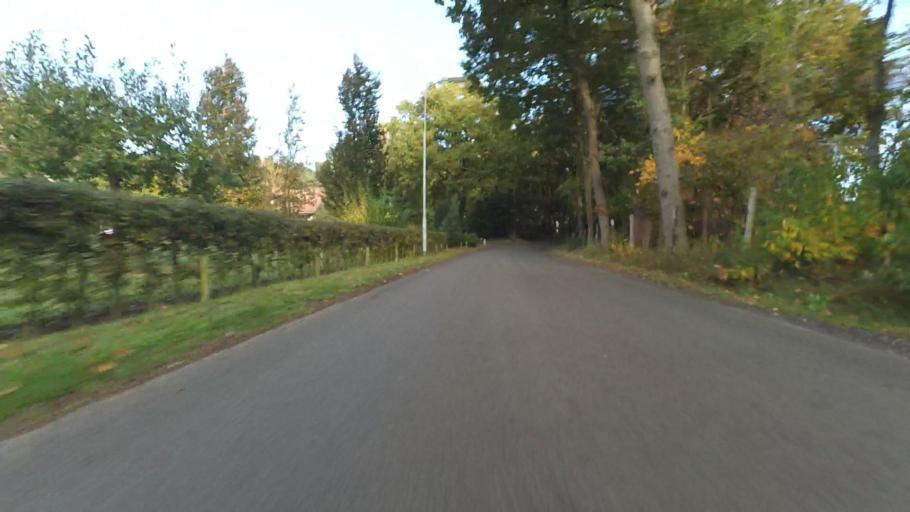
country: NL
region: Gelderland
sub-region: Gemeente Ermelo
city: Horst
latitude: 52.3200
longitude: 5.5878
